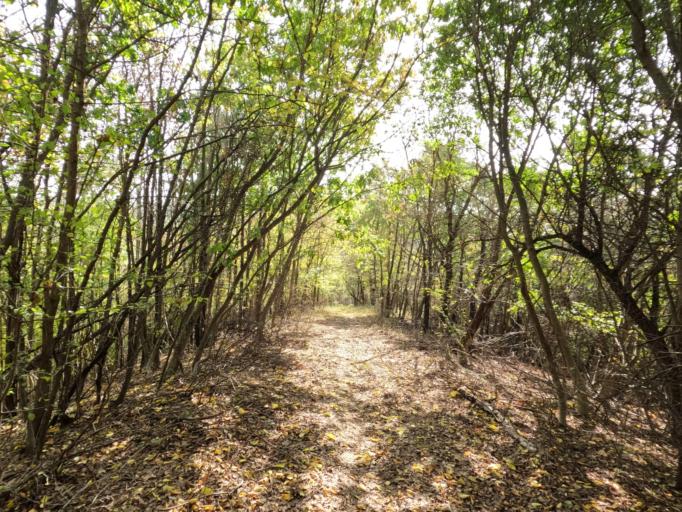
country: HU
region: Tolna
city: Szentgalpuszta
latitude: 46.3445
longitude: 18.6288
